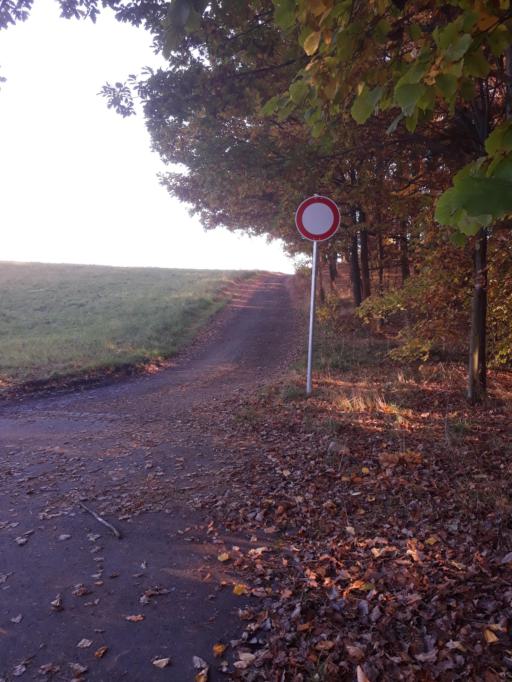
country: DE
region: Saxony
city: Reinsdorf
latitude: 50.6807
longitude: 12.5680
